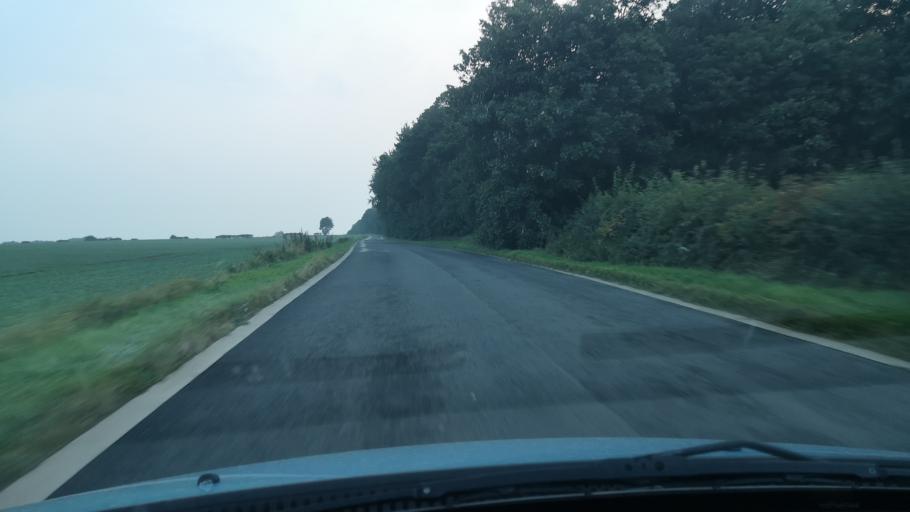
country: GB
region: England
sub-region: Doncaster
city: Norton
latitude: 53.6200
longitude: -1.2160
